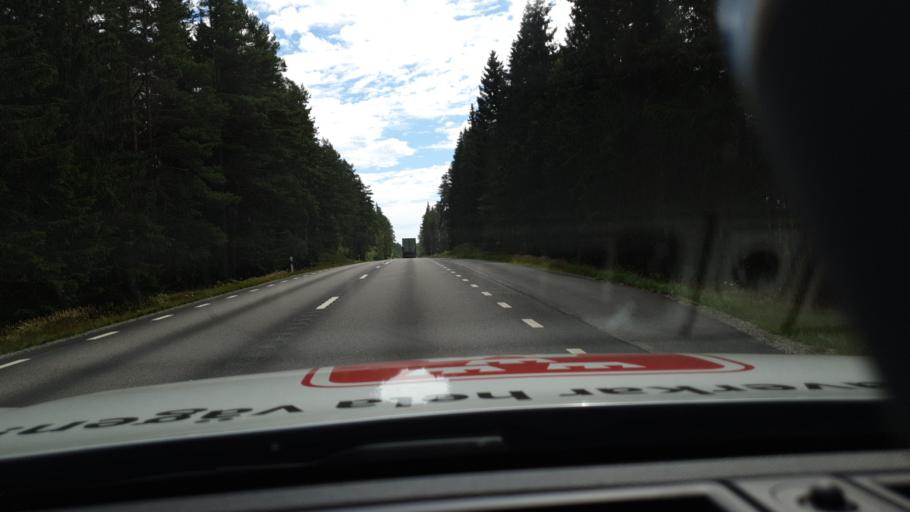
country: SE
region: Joenkoeping
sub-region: Savsjo Kommun
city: Vrigstad
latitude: 57.3257
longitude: 14.4785
